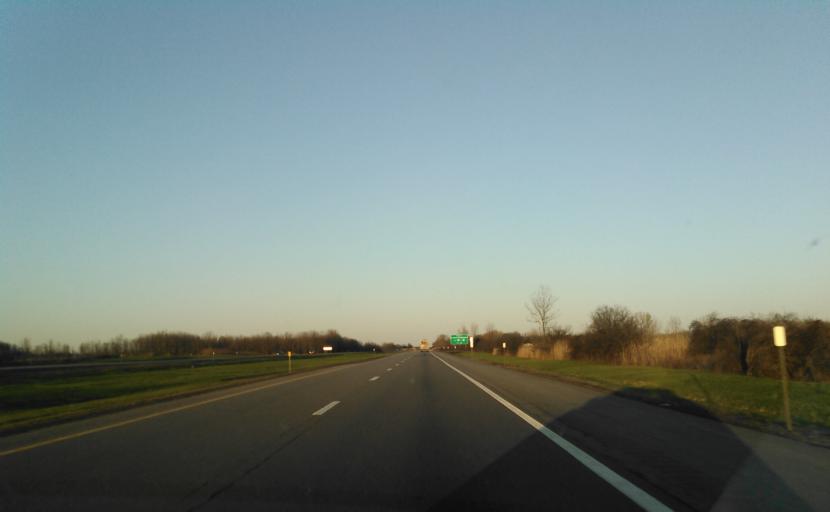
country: US
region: New York
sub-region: Ontario County
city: Clifton Springs
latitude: 42.9732
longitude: -77.1331
